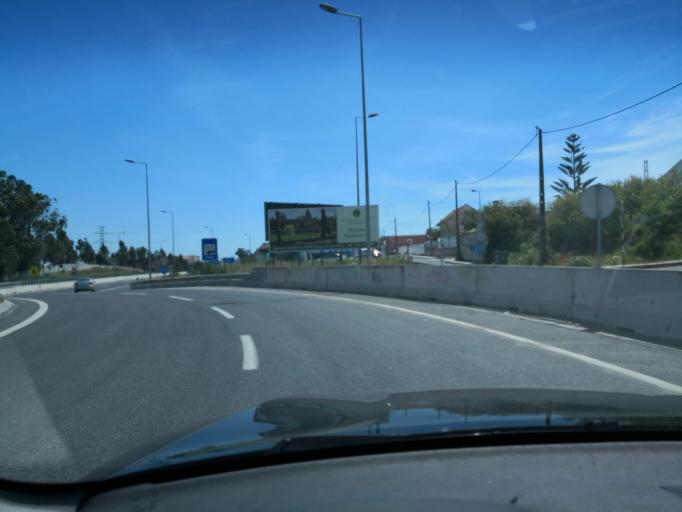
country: PT
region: Setubal
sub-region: Almada
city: Caparica
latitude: 38.6550
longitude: -9.2010
